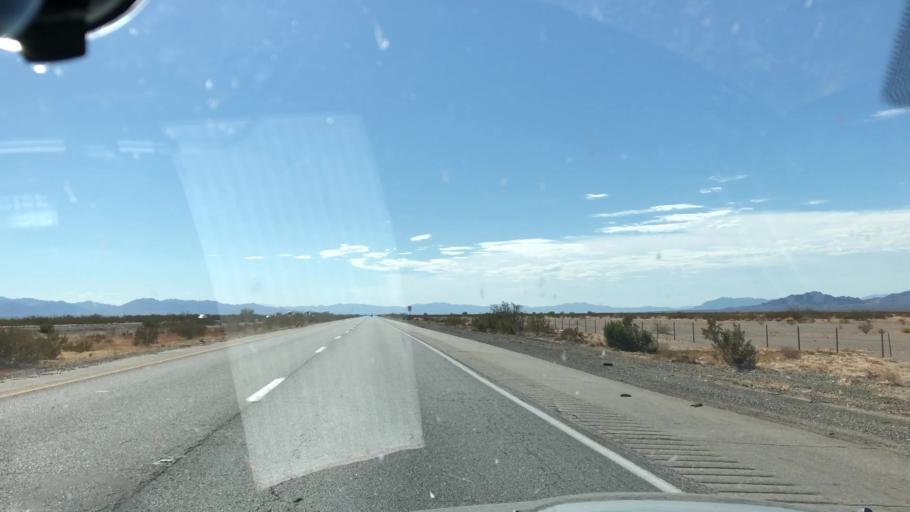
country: US
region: California
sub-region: Riverside County
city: Mesa Verde
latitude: 33.6115
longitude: -115.0031
